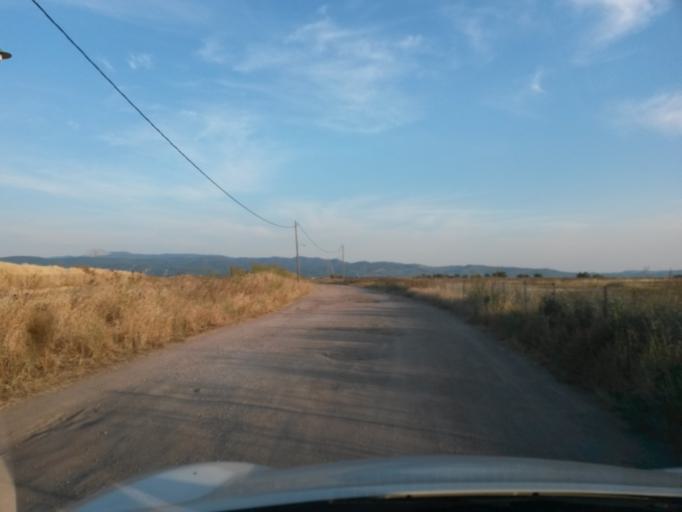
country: GR
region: North Aegean
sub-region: Nomos Lesvou
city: Kalloni
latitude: 39.2098
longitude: 26.2450
